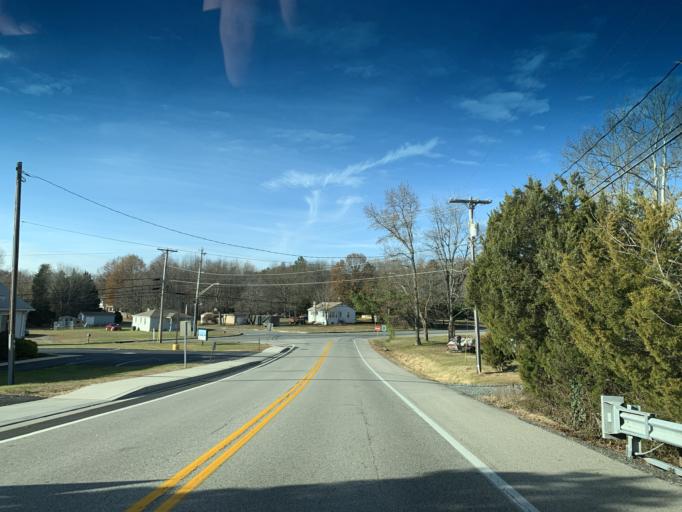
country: US
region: Maryland
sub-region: Cecil County
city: Charlestown
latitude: 39.5827
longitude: -75.9712
